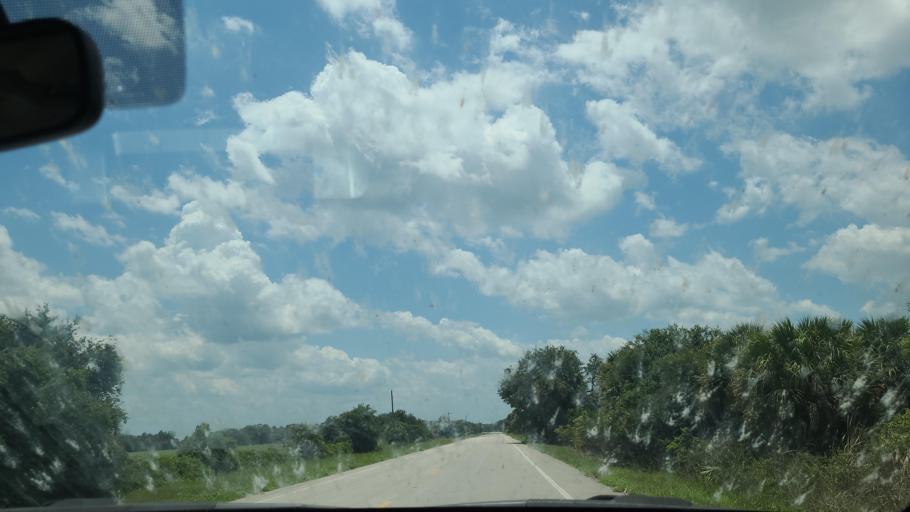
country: US
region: Florida
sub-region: Glades County
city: Buckhead Ridge
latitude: 27.1512
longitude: -81.0941
